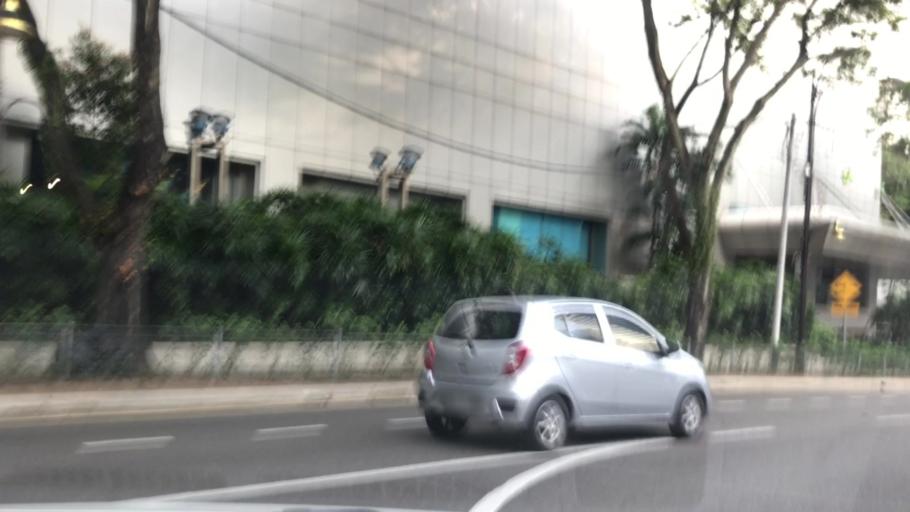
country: MY
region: Kuala Lumpur
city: Kuala Lumpur
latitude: 3.1515
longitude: 101.7067
